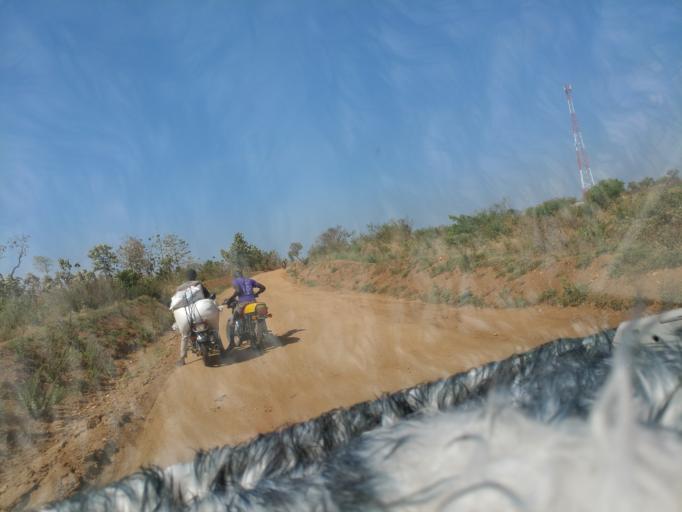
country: UG
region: Northern Region
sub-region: Yumbe District
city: Yumbe
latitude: 3.3907
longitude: 31.3376
